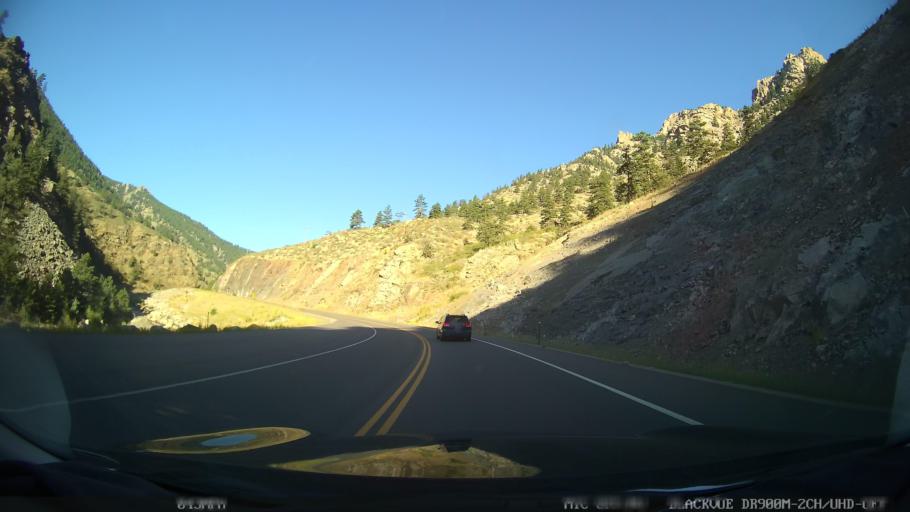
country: US
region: Colorado
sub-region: Boulder County
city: Lyons
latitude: 40.4289
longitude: -105.3084
